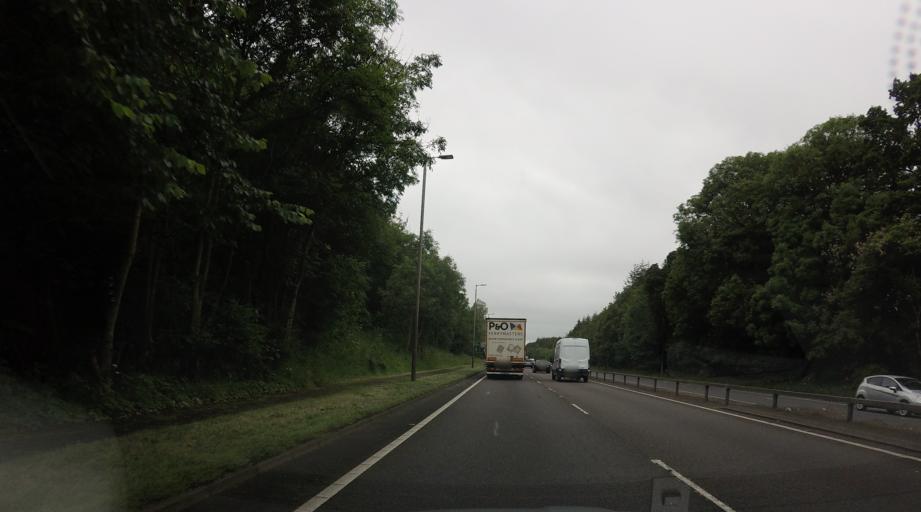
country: GB
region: Scotland
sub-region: South Lanarkshire
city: High Blantyre
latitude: 55.7817
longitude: -4.1386
